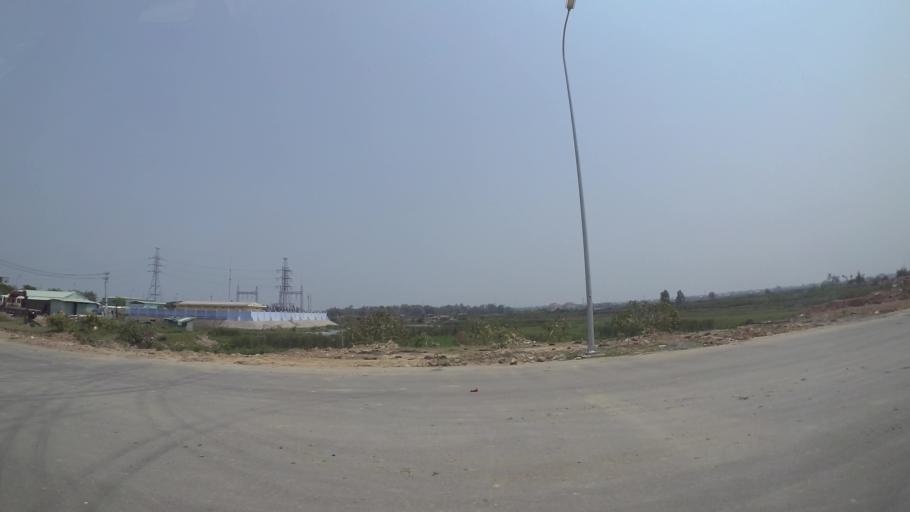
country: VN
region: Da Nang
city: Cam Le
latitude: 16.0005
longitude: 108.2248
